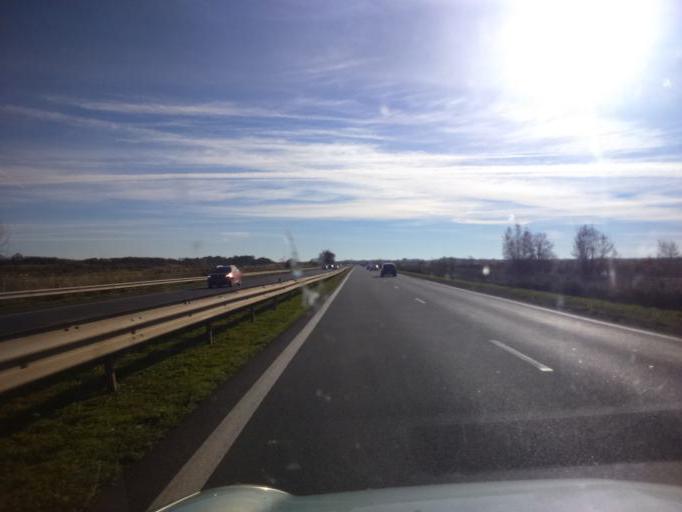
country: FR
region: Poitou-Charentes
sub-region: Departement de la Charente-Maritime
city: Saint-Laurent-de-la-Pree
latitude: 45.9852
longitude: -1.0256
